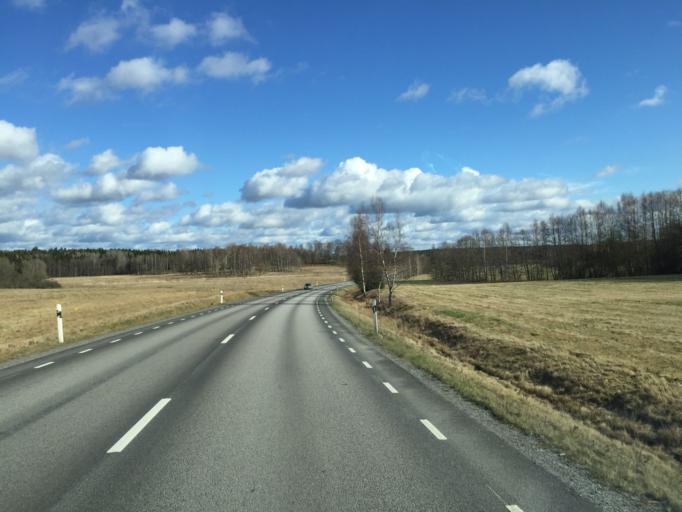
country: SE
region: Stockholm
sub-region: Sodertalje Kommun
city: Soedertaelje
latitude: 59.2281
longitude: 17.5587
